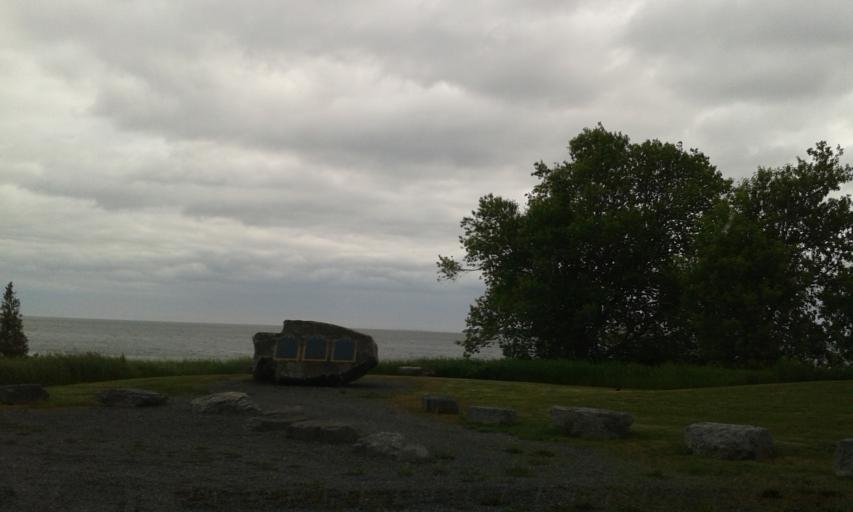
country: CA
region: Ontario
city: Skatepark
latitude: 44.1478
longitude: -76.8389
